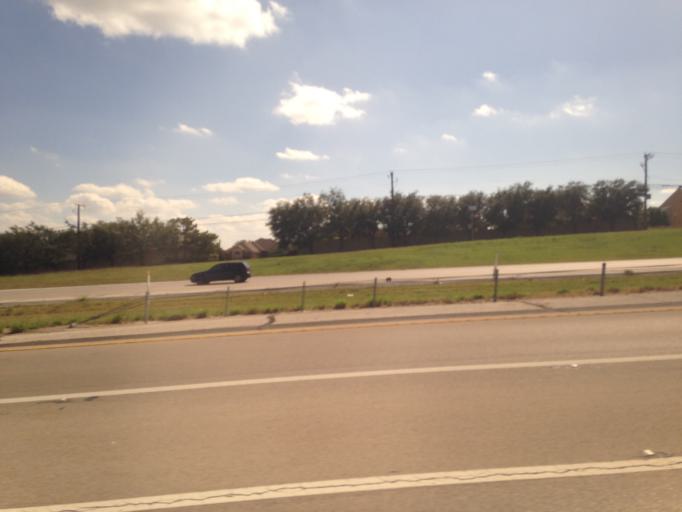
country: US
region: Texas
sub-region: Tarrant County
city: White Settlement
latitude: 32.7211
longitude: -97.5226
